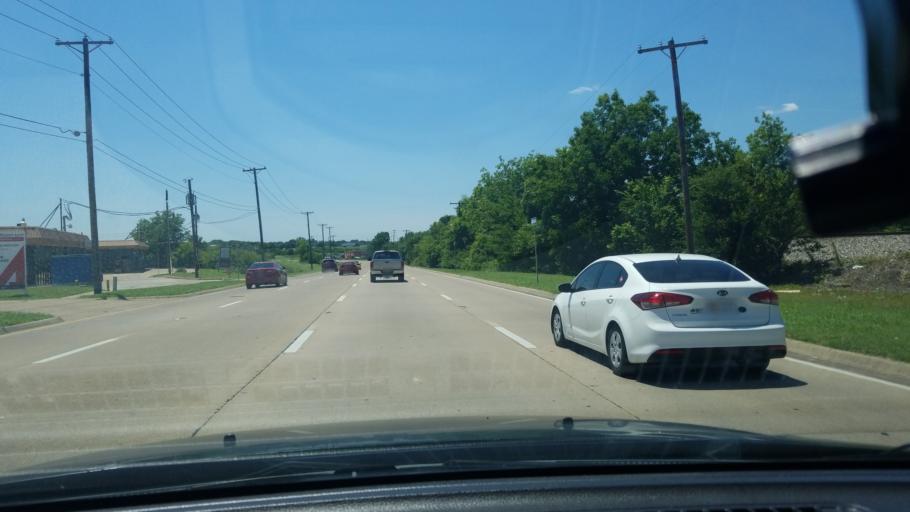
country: US
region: Texas
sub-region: Dallas County
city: Mesquite
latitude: 32.7691
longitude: -96.6145
